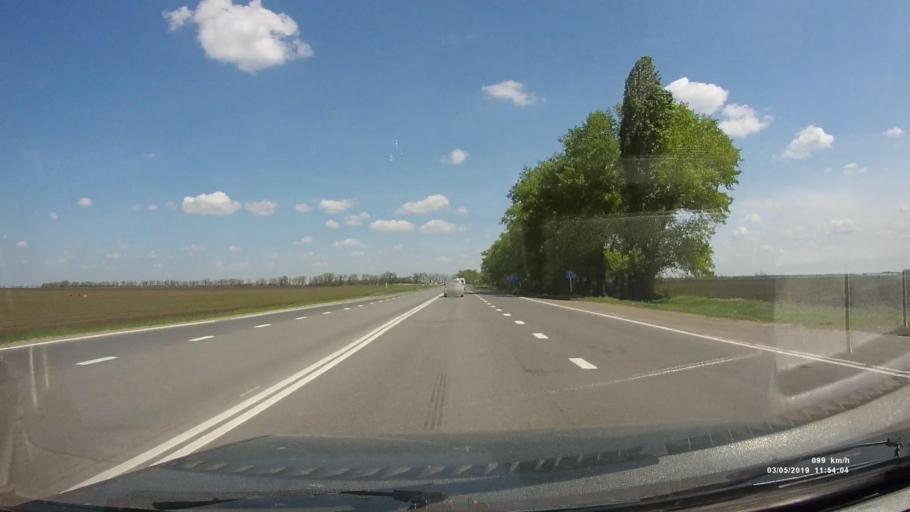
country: RU
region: Rostov
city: Bagayevskaya
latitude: 47.1679
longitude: 40.2730
